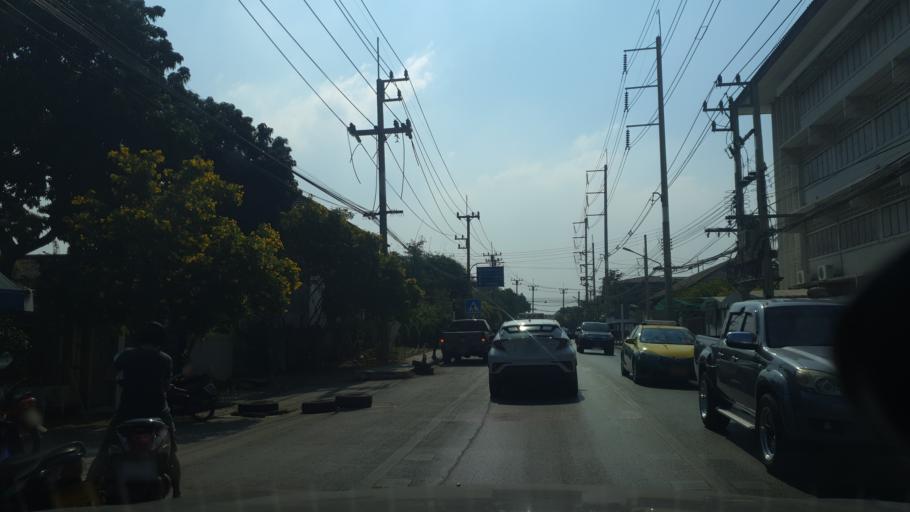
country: TH
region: Nakhon Pathom
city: Salaya
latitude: 13.7719
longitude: 100.2855
